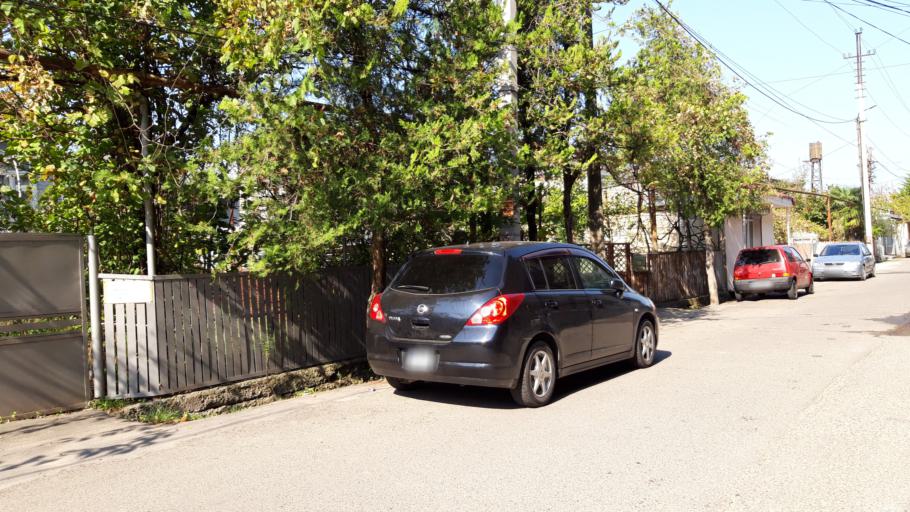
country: GE
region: Imereti
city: Samtredia
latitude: 42.1623
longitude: 42.3417
